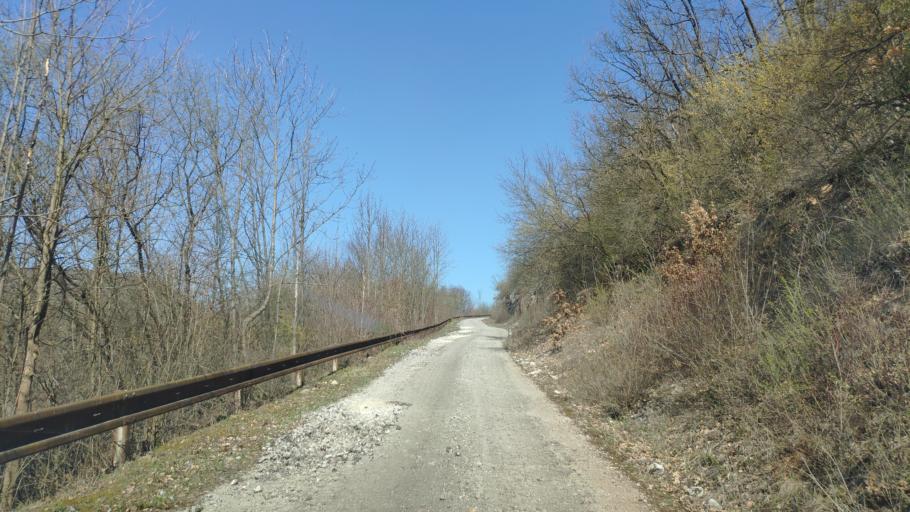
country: SK
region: Kosicky
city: Roznava
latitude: 48.5633
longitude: 20.4030
